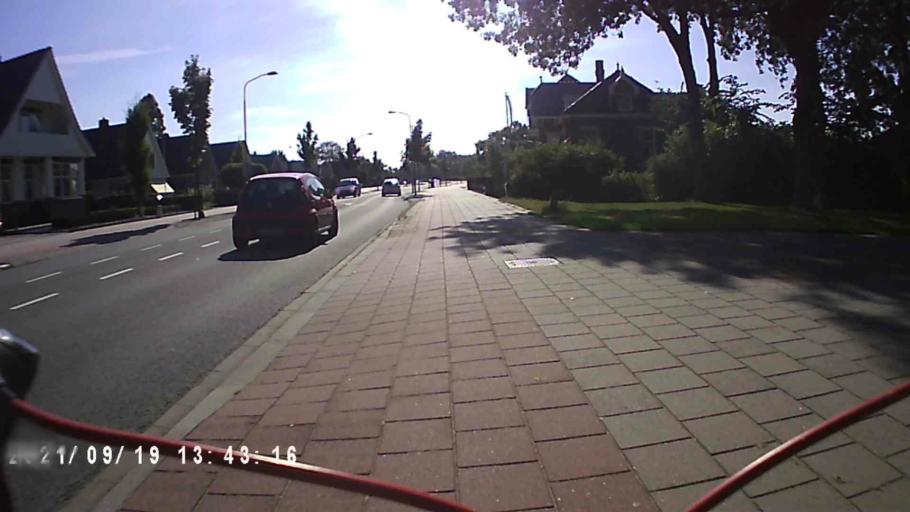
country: NL
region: Groningen
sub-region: Gemeente  Oldambt
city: Winschoten
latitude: 53.1360
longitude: 7.0426
